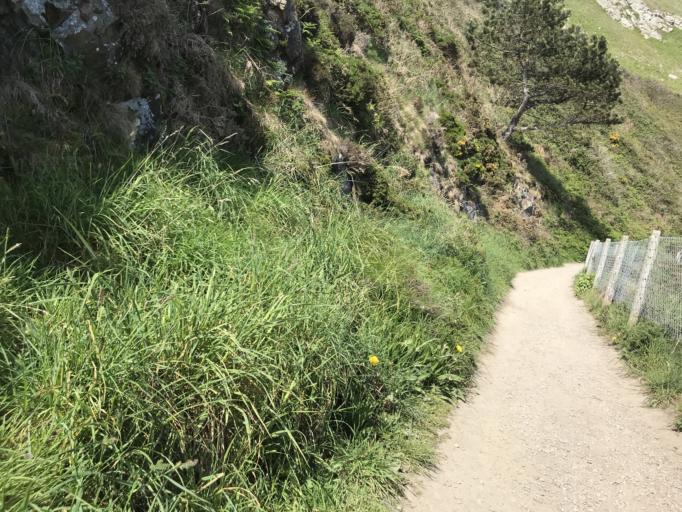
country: IE
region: Leinster
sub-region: Wicklow
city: Bray
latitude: 53.1828
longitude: -6.0770
